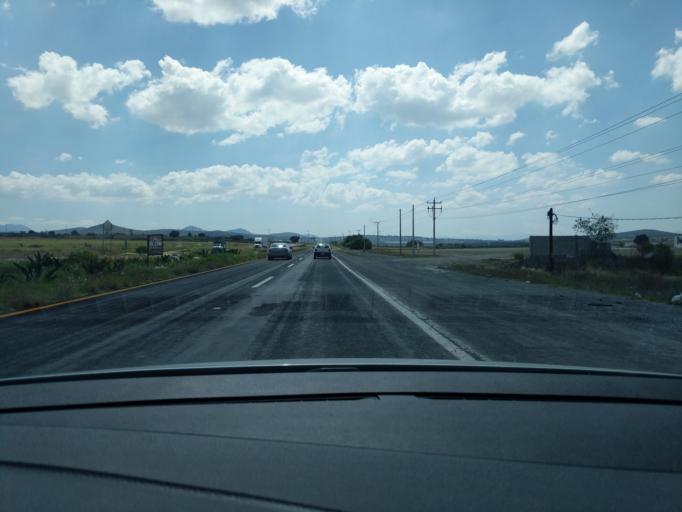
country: MX
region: Hidalgo
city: Zempoala
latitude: 19.9569
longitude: -98.6936
